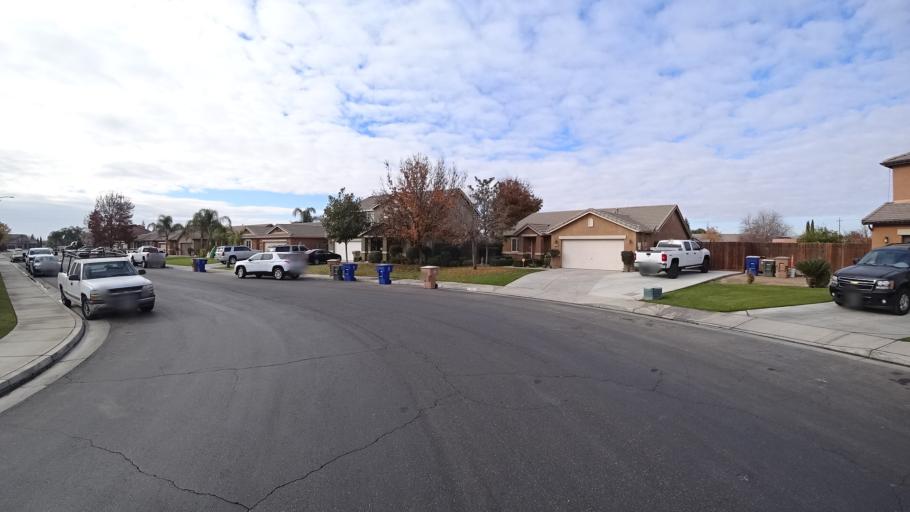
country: US
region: California
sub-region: Kern County
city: Rosedale
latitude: 35.3026
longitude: -119.1317
